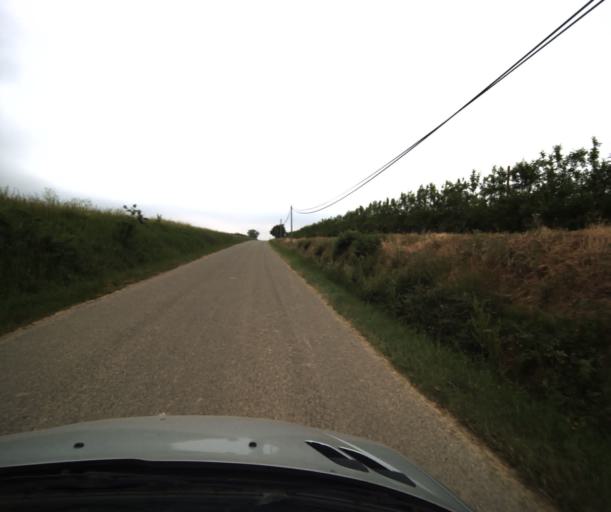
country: FR
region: Midi-Pyrenees
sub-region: Departement du Tarn-et-Garonne
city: Saint-Nicolas-de-la-Grave
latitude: 44.0574
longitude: 0.9867
